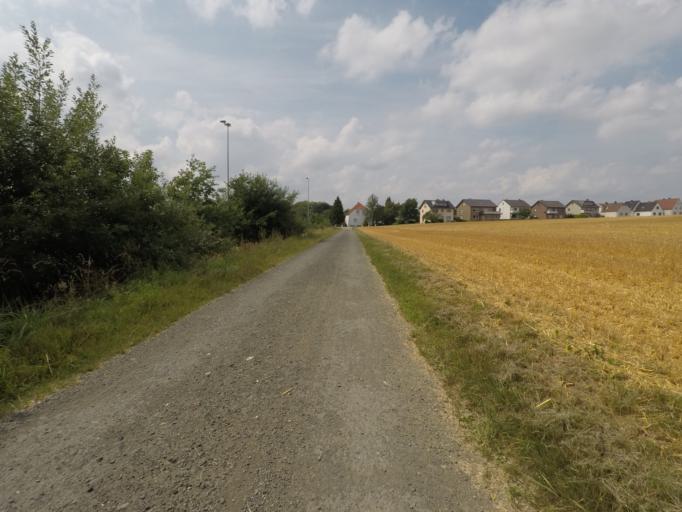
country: DE
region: North Rhine-Westphalia
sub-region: Regierungsbezirk Detmold
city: Hiddenhausen
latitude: 52.1544
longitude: 8.5882
